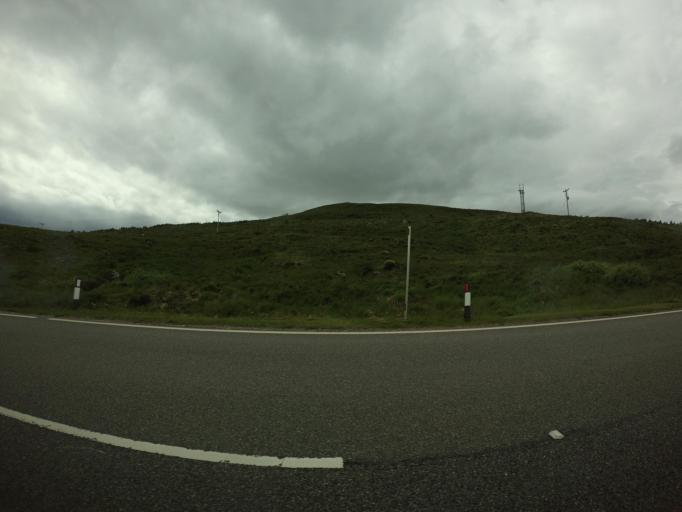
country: GB
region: Scotland
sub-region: Highland
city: Muir of Ord
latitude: 57.6999
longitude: -4.8099
